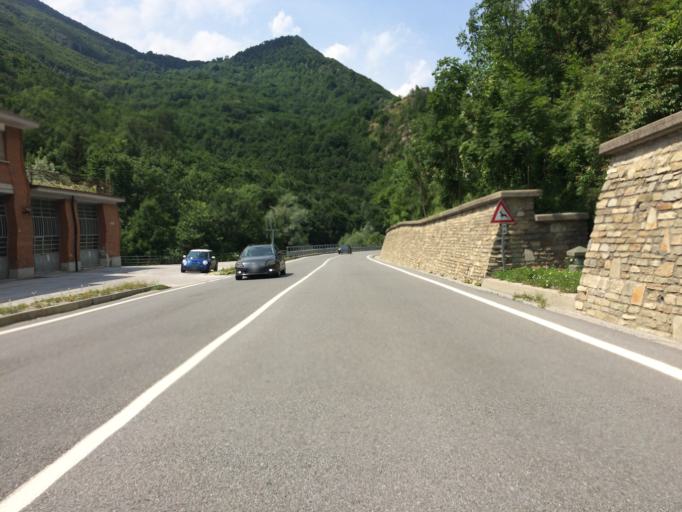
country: IT
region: Piedmont
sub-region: Provincia di Cuneo
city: Limone Piemonte
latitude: 44.2090
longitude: 7.5734
